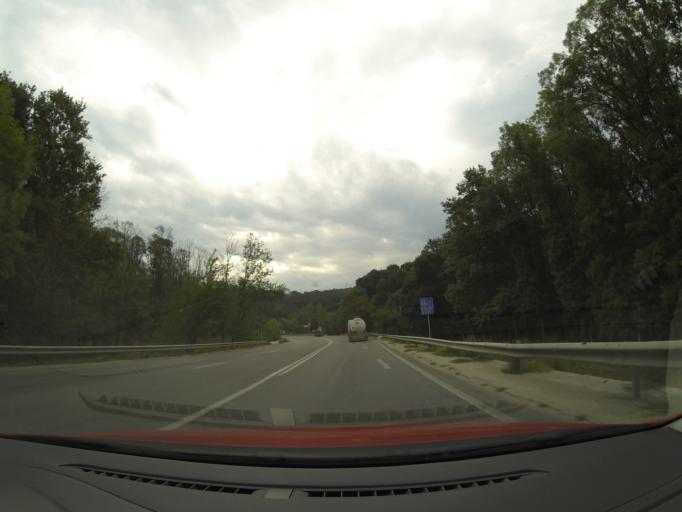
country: RO
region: Olt
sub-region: Comuna Barza
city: Branet
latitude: 44.3604
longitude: 24.1857
